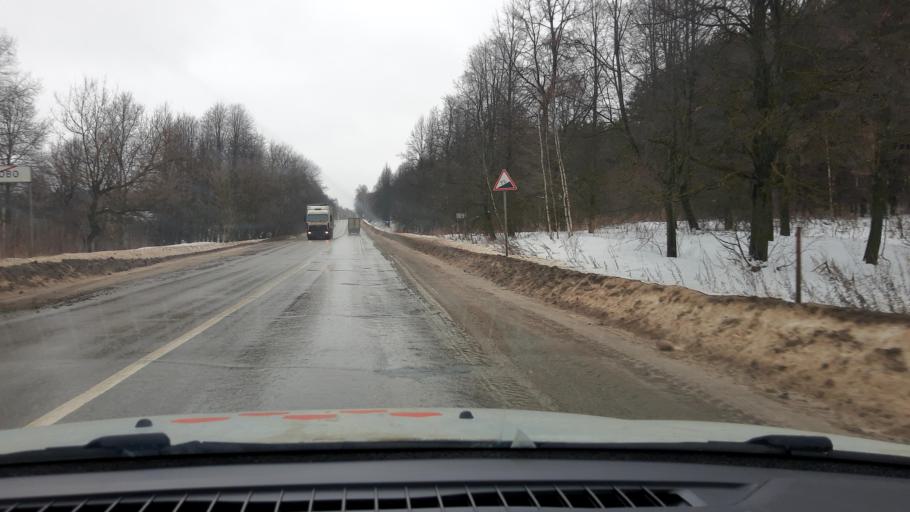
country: RU
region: Nizjnij Novgorod
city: Pavlovo
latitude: 55.9669
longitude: 43.1212
